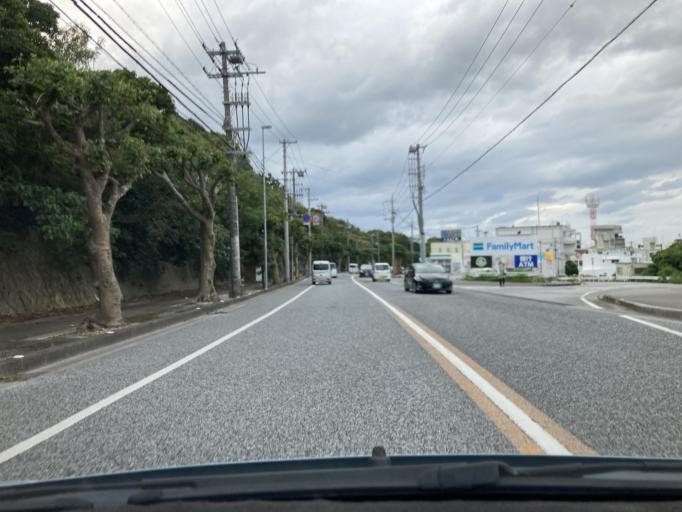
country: JP
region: Okinawa
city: Tomigusuku
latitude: 26.1746
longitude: 127.6884
